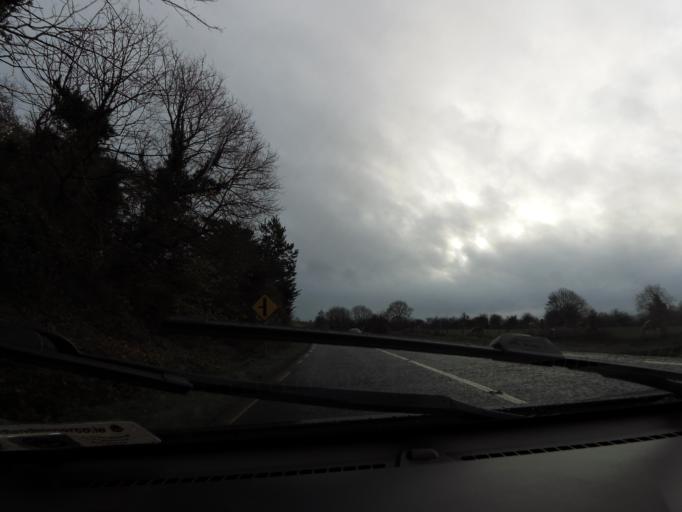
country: IE
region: Munster
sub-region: North Tipperary
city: Roscrea
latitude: 52.9869
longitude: -7.8552
